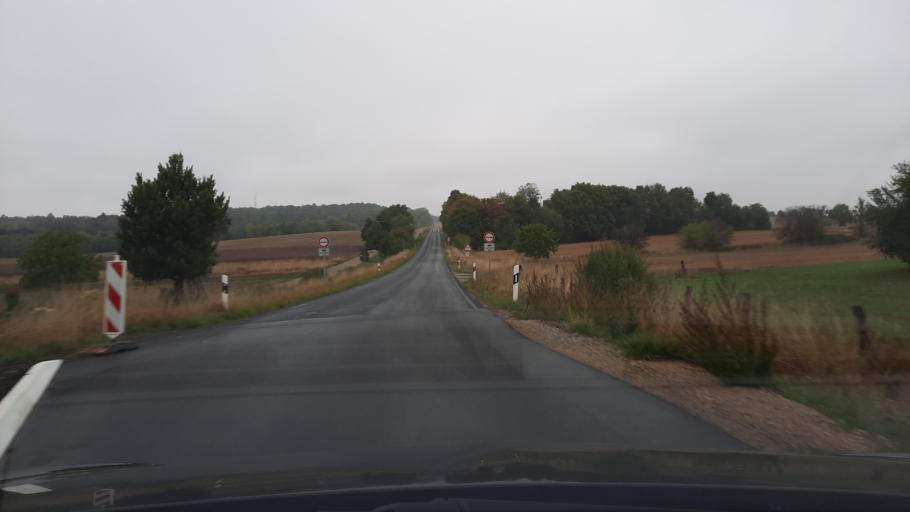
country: DE
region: Rheinland-Pfalz
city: Bitburg
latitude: 49.9811
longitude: 6.5268
